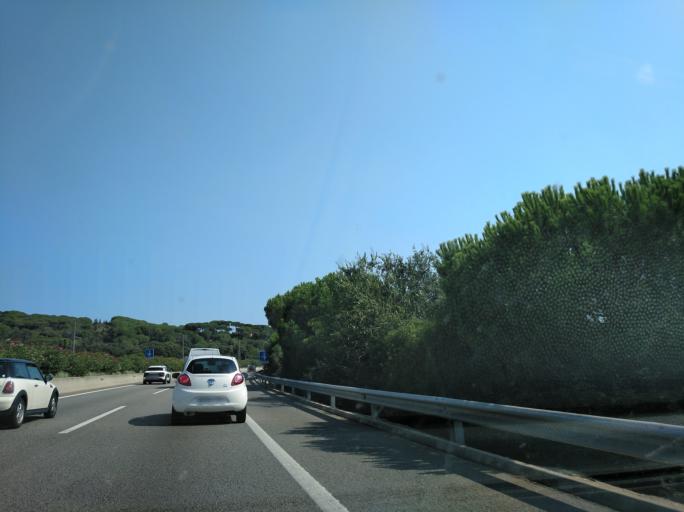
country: ES
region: Catalonia
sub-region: Provincia de Barcelona
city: Argentona
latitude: 41.5586
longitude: 2.4066
